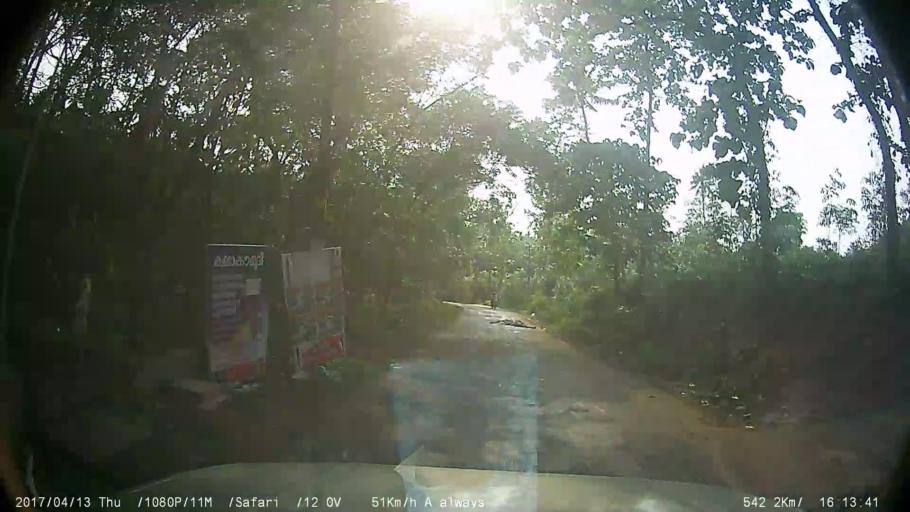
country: IN
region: Kerala
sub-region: Ernakulam
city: Piravam
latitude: 9.8228
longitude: 76.5111
